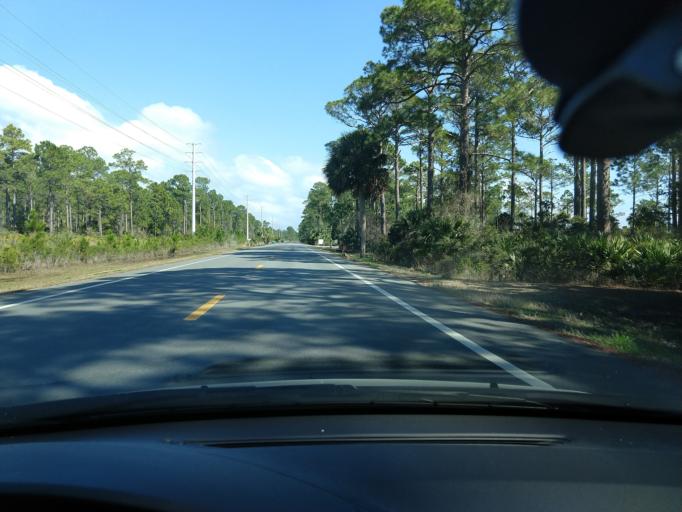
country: US
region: Florida
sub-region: Gulf County
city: Port Saint Joe
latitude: 29.6918
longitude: -85.2470
